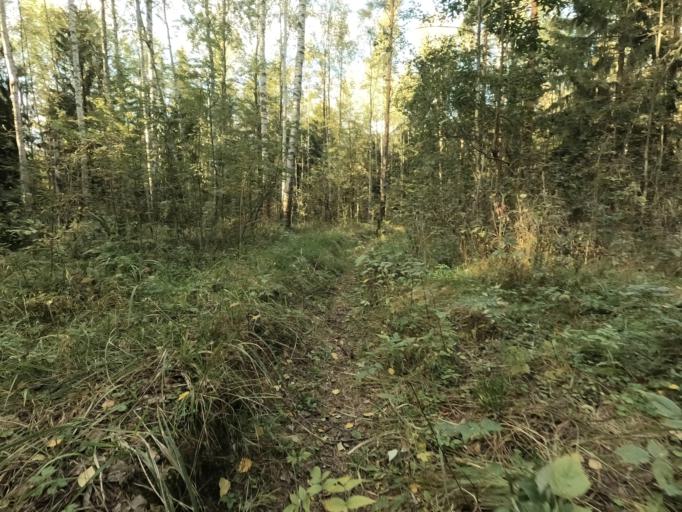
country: RU
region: Leningrad
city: Imeni Sverdlova
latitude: 59.8516
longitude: 30.7286
